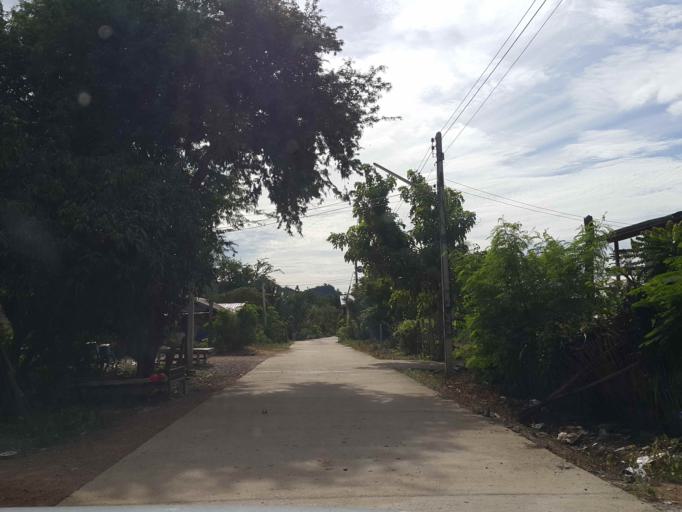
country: TH
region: Sukhothai
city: Thung Saliam
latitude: 17.2286
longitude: 99.5159
